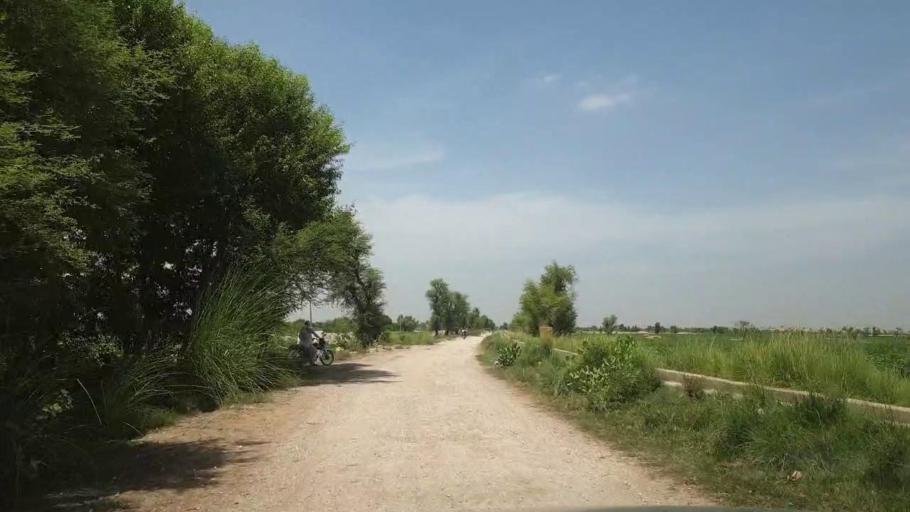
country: PK
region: Sindh
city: Kot Diji
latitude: 27.1358
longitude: 69.0447
